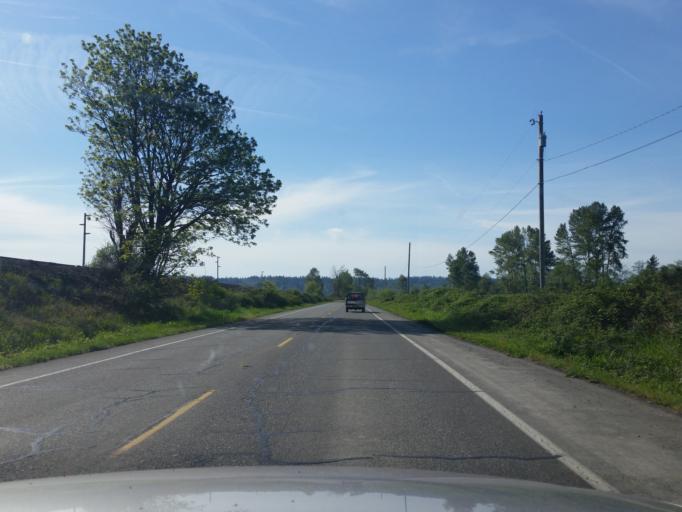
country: US
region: Washington
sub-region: Snohomish County
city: Fobes Hill
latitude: 47.9196
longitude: -122.1445
